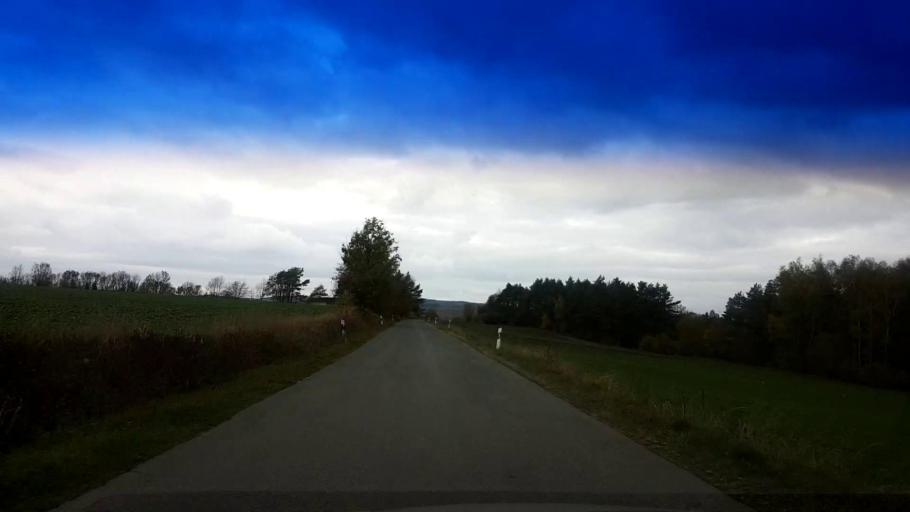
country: DE
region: Bavaria
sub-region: Upper Franconia
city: Wattendorf
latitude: 50.0197
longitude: 11.1150
